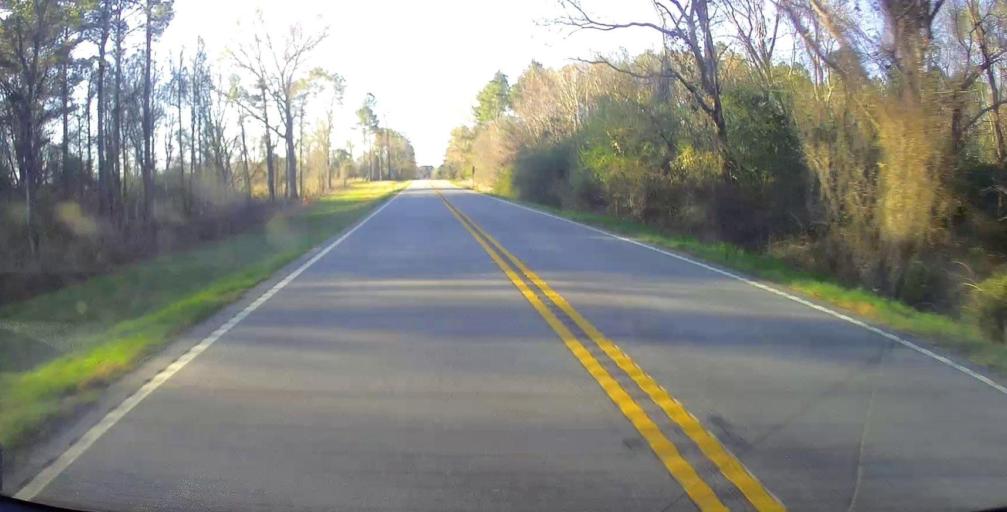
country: US
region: Georgia
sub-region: Wilcox County
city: Abbeville
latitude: 32.1281
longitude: -83.3337
